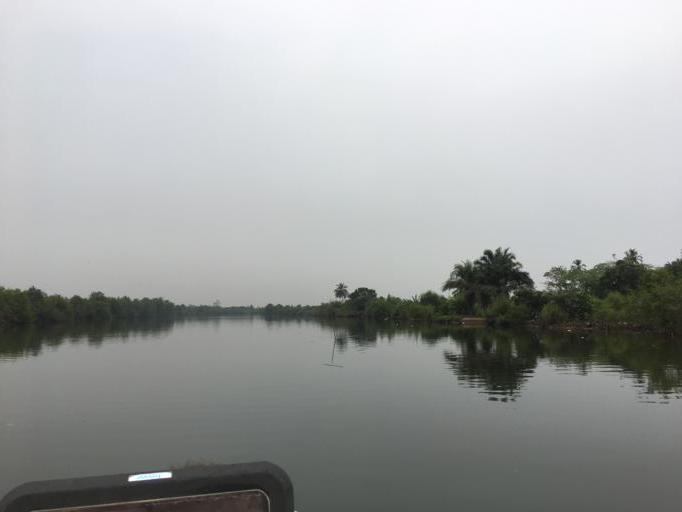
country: LR
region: Montserrado
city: Monrovia
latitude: 6.3691
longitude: -10.7771
